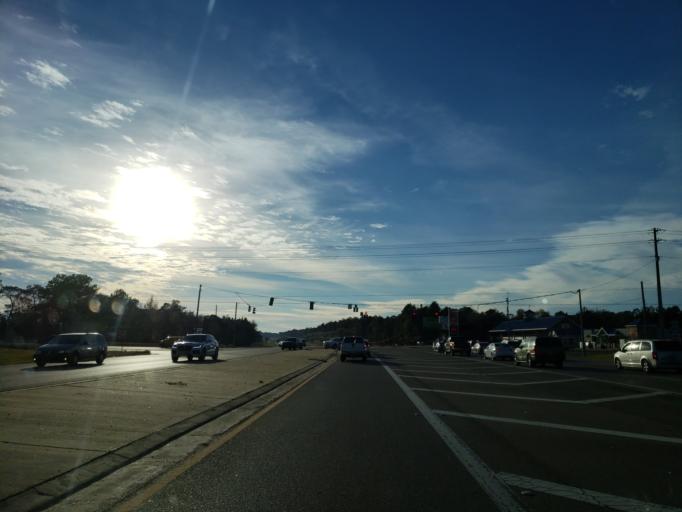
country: US
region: Mississippi
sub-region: Lamar County
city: West Hattiesburg
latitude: 31.3129
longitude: -89.4711
